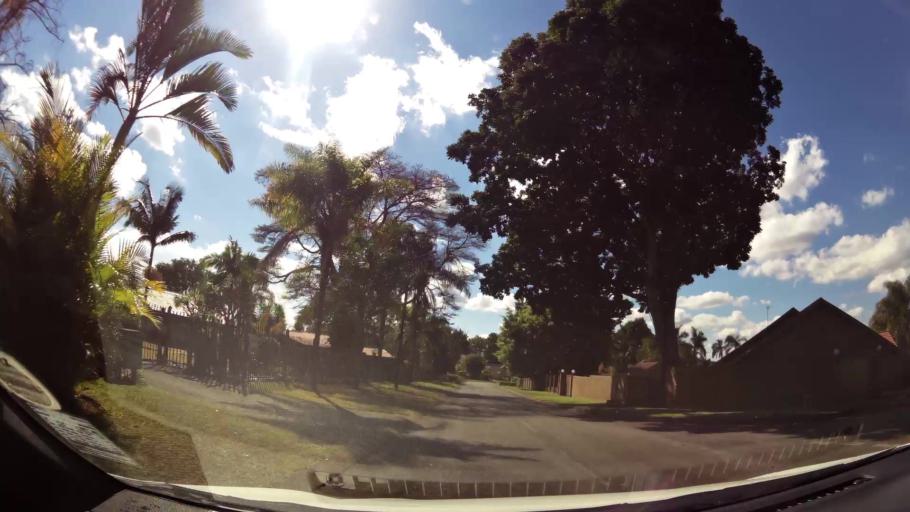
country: ZA
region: Limpopo
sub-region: Mopani District Municipality
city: Tzaneen
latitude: -23.8190
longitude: 30.1461
